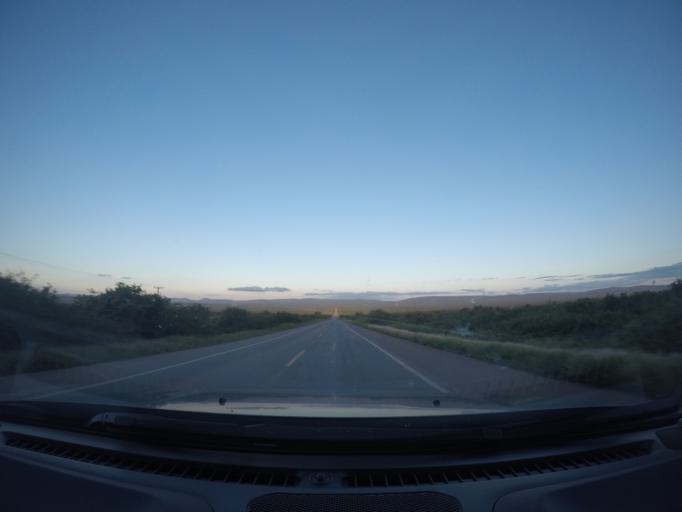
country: BR
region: Bahia
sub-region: Seabra
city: Seabra
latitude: -12.4110
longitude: -41.9708
